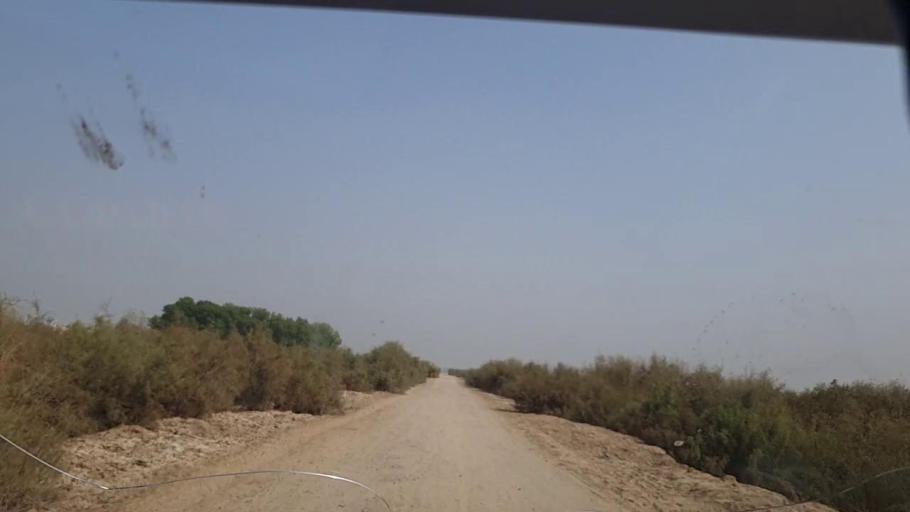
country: PK
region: Sindh
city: Shikarpur
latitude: 28.0383
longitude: 68.6420
